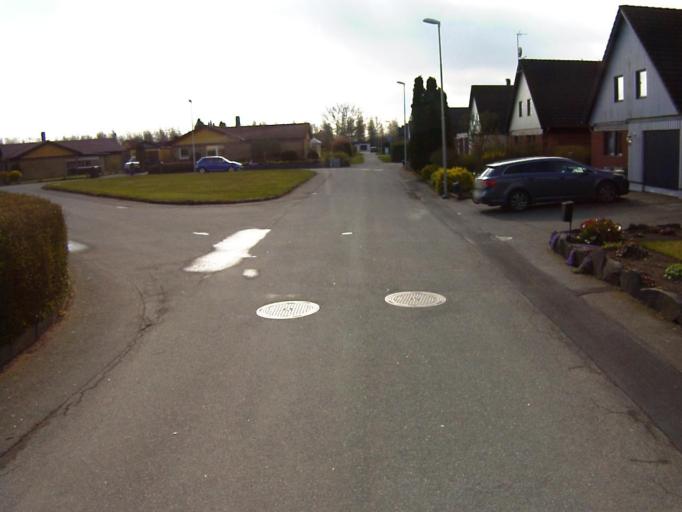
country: SE
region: Skane
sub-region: Kristianstads Kommun
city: Kristianstad
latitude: 56.0099
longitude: 14.1047
